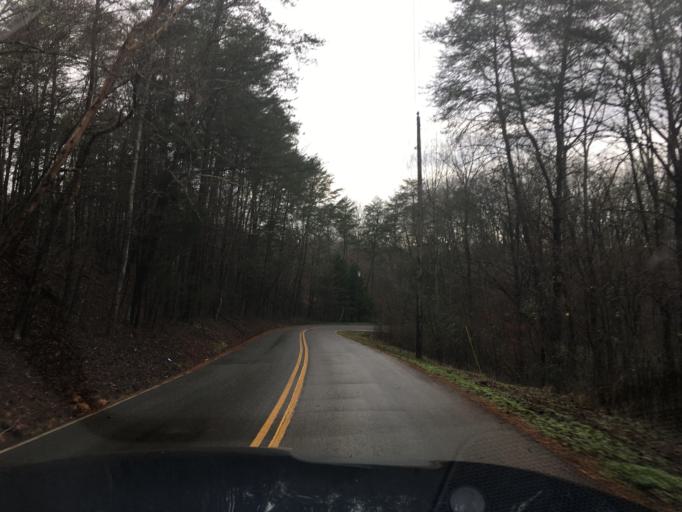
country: US
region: Tennessee
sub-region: McMinn County
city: Englewood
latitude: 35.3629
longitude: -84.4247
